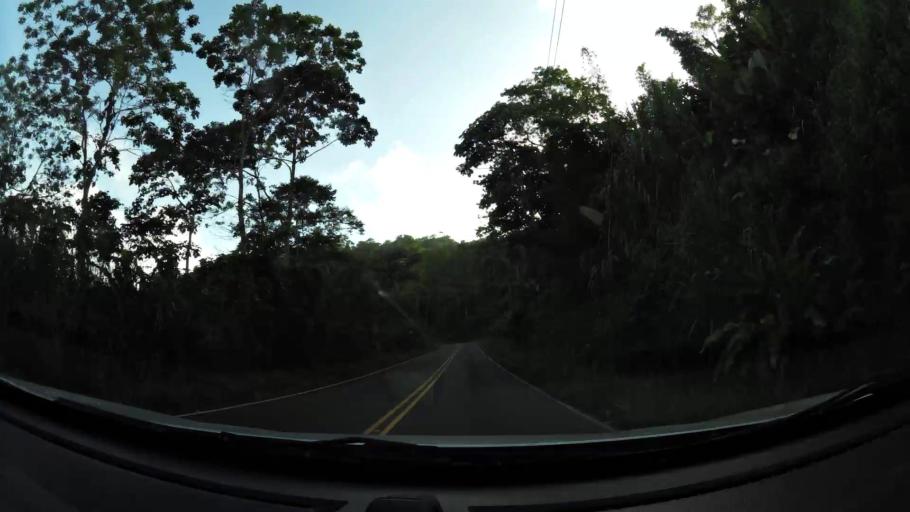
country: CR
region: Limon
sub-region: Canton de Siquirres
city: Siquirres
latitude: 10.0537
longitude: -83.5513
